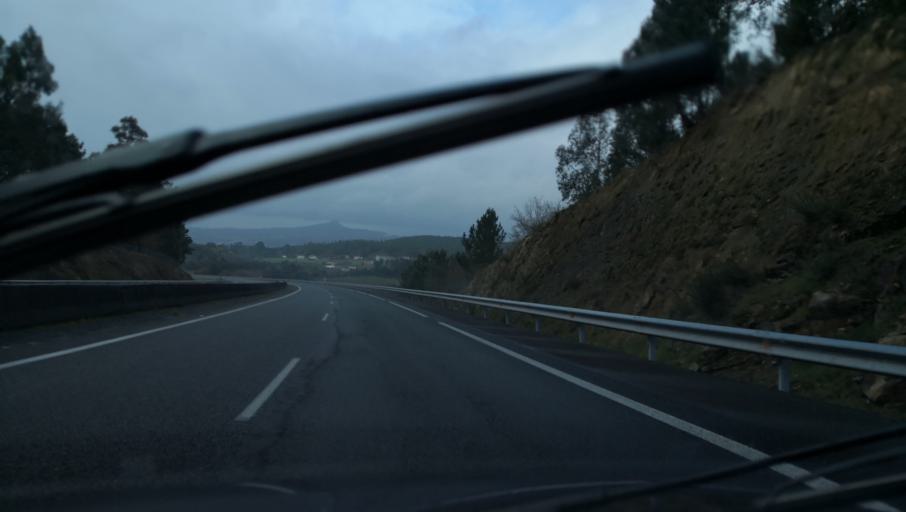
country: ES
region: Galicia
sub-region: Provincia da Coruna
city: Ribeira
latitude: 42.7418
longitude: -8.3718
